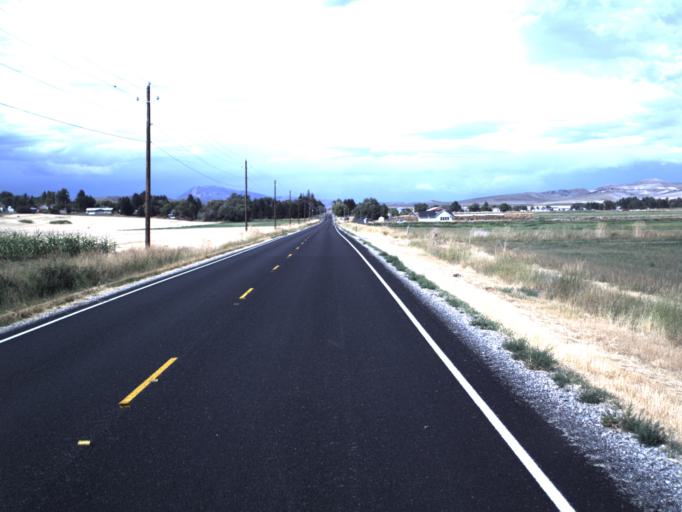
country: US
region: Utah
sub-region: Cache County
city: Benson
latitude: 41.9073
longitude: -112.0455
